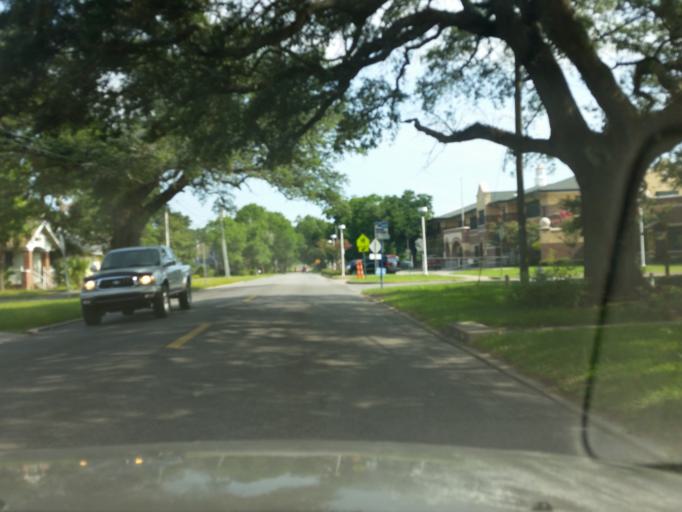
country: US
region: Florida
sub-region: Escambia County
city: Pensacola
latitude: 30.4282
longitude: -87.2037
